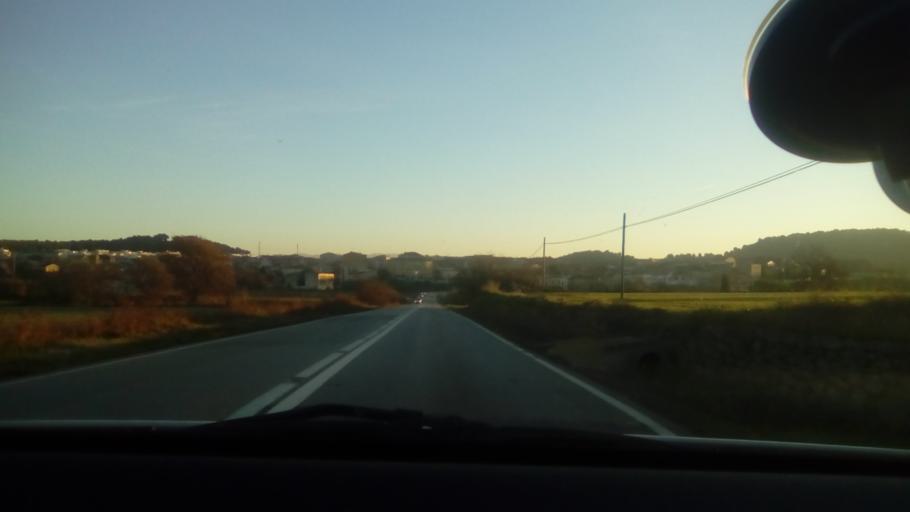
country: ES
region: Catalonia
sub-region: Provincia de Barcelona
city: Sant Fruitos de Bages
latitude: 41.7477
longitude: 1.8656
